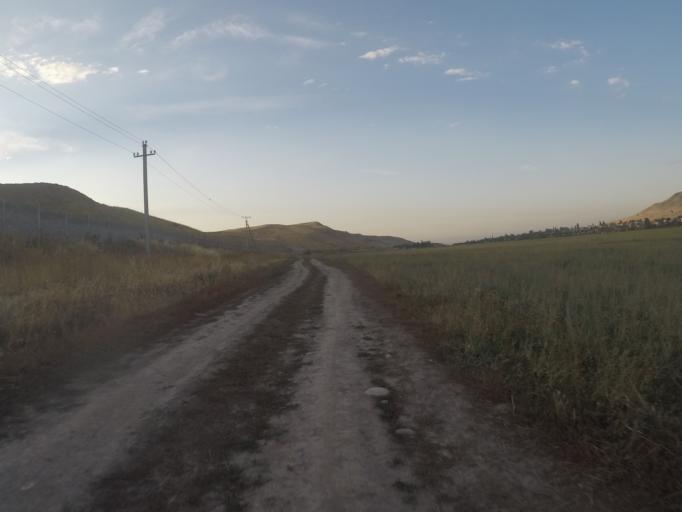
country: KG
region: Chuy
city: Bishkek
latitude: 42.7560
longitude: 74.6363
